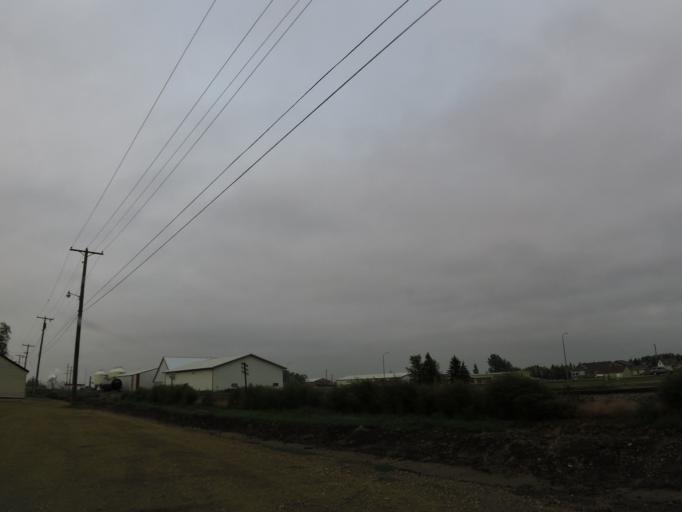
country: US
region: North Dakota
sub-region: Walsh County
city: Grafton
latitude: 48.5683
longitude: -97.1795
